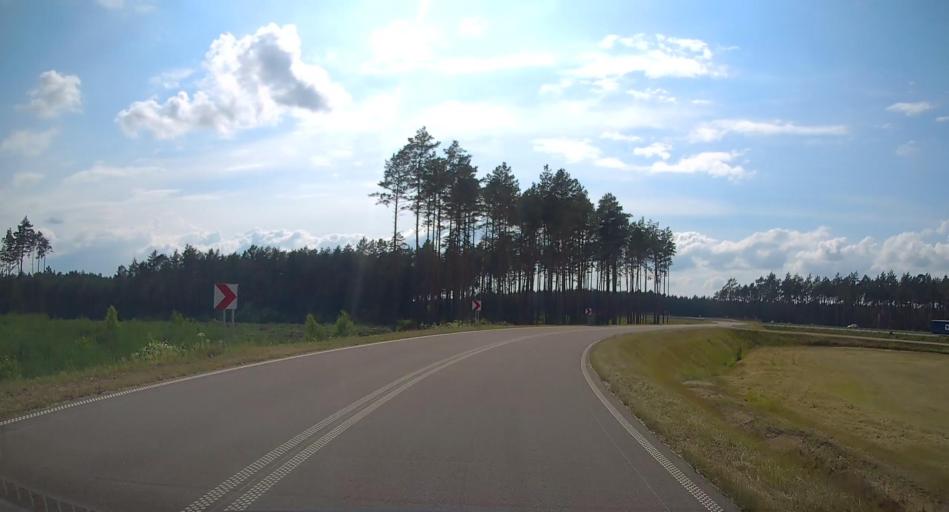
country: PL
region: Masovian Voivodeship
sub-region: Powiat ostrowski
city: Brok
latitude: 52.7345
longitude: 21.7474
